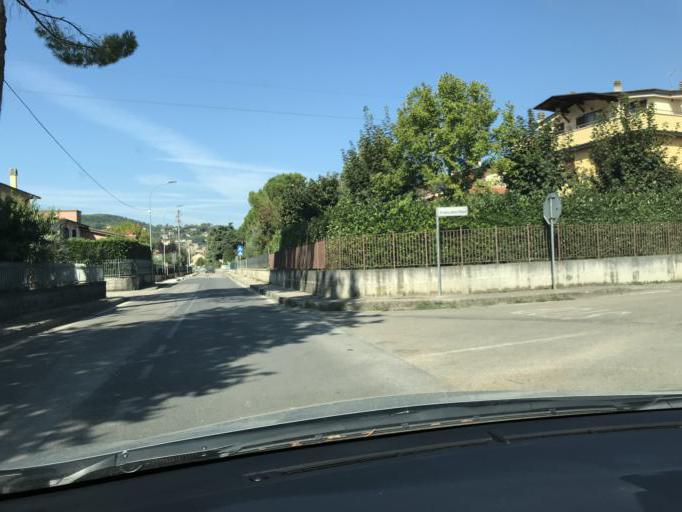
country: IT
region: Umbria
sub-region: Provincia di Perugia
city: Ponte Felcino
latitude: 43.1087
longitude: 12.4554
